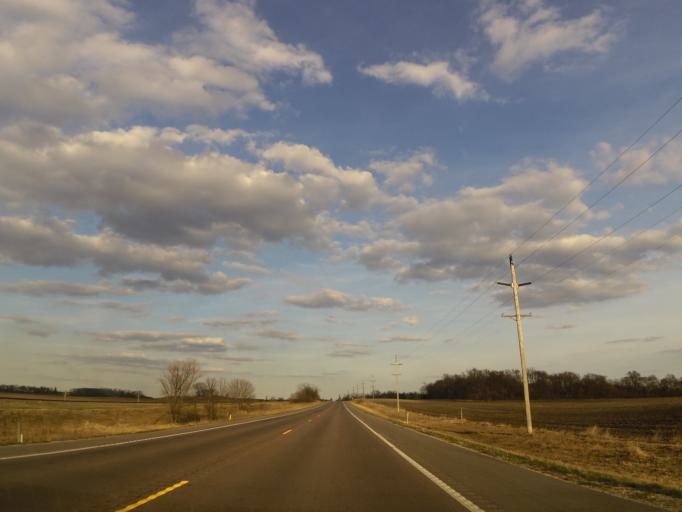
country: US
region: Minnesota
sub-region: Renville County
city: Hector
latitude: 44.7246
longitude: -94.5381
